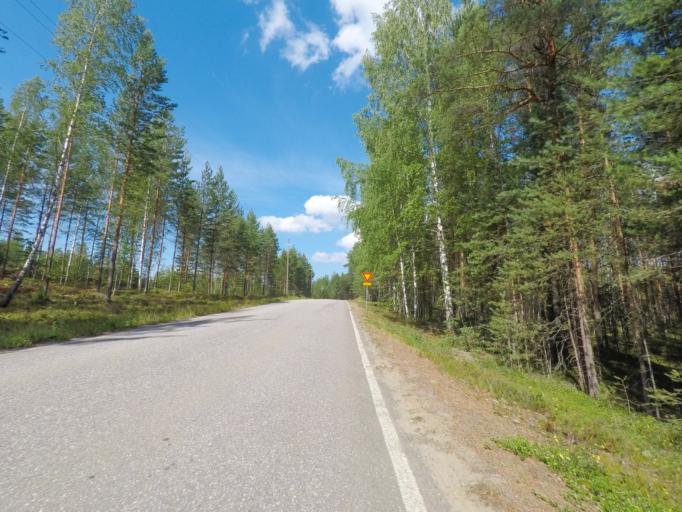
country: FI
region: Southern Savonia
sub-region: Mikkeli
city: Puumala
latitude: 61.4583
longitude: 28.1748
